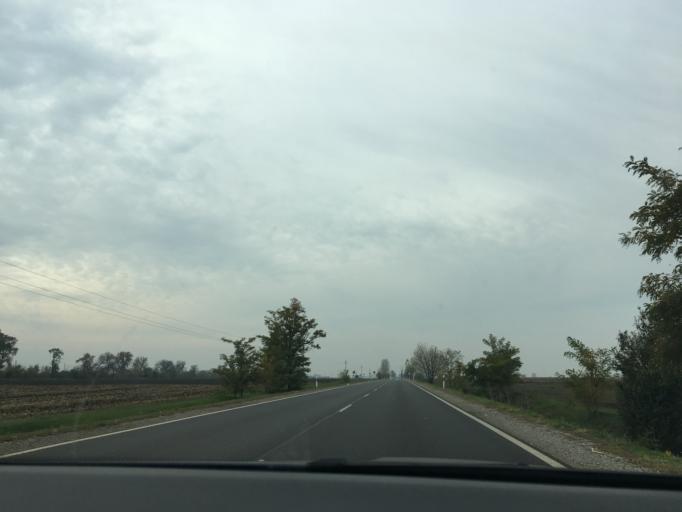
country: HU
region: Hajdu-Bihar
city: Kaba
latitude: 47.3625
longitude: 21.2398
